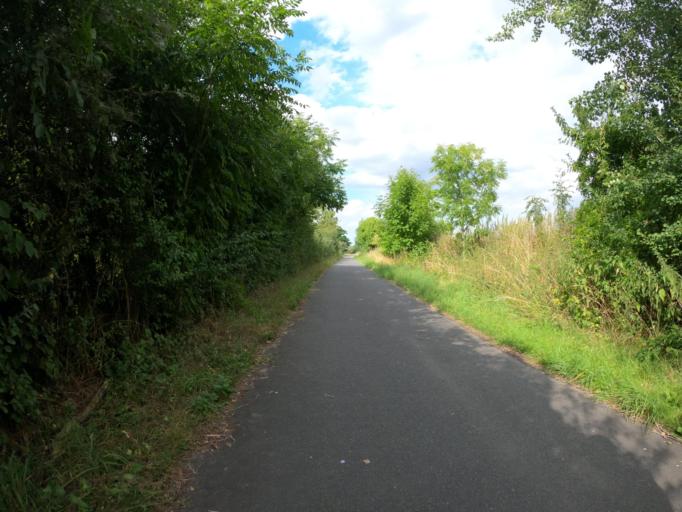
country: DE
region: Mecklenburg-Vorpommern
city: Woldegk
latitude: 53.3857
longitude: 13.5898
